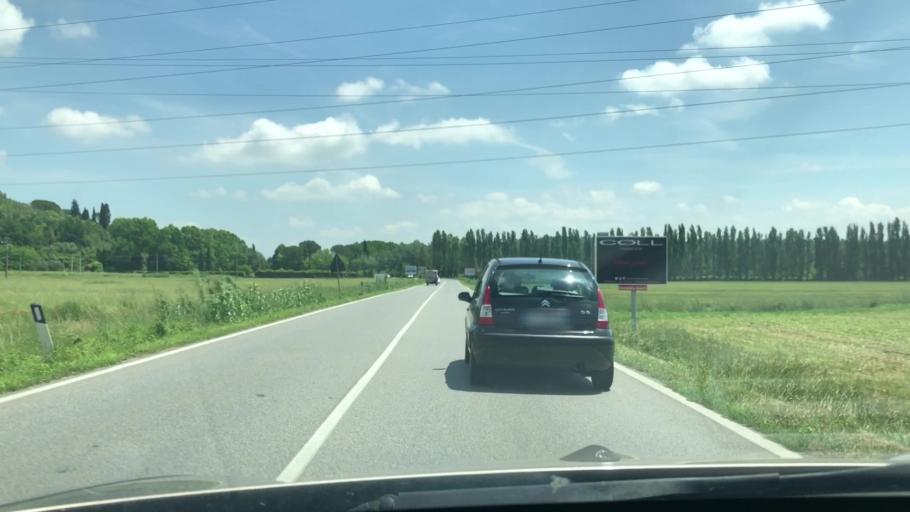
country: IT
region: Tuscany
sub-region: Province of Pisa
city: Treggiaia
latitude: 43.6175
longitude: 10.6759
